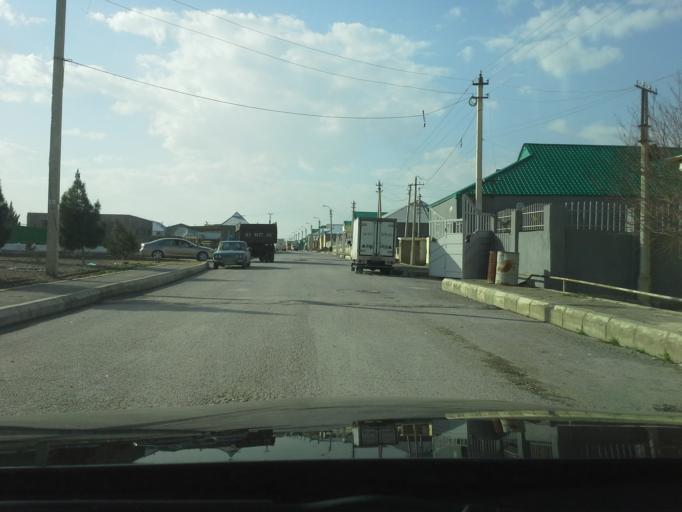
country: TM
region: Ahal
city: Abadan
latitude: 38.0196
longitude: 58.2251
